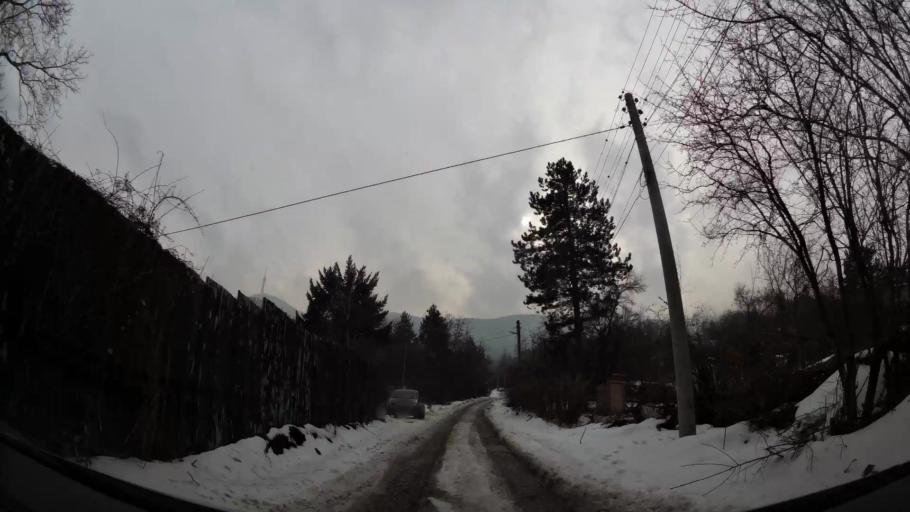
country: BG
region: Sofia-Capital
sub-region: Stolichna Obshtina
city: Sofia
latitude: 42.6502
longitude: 23.2315
